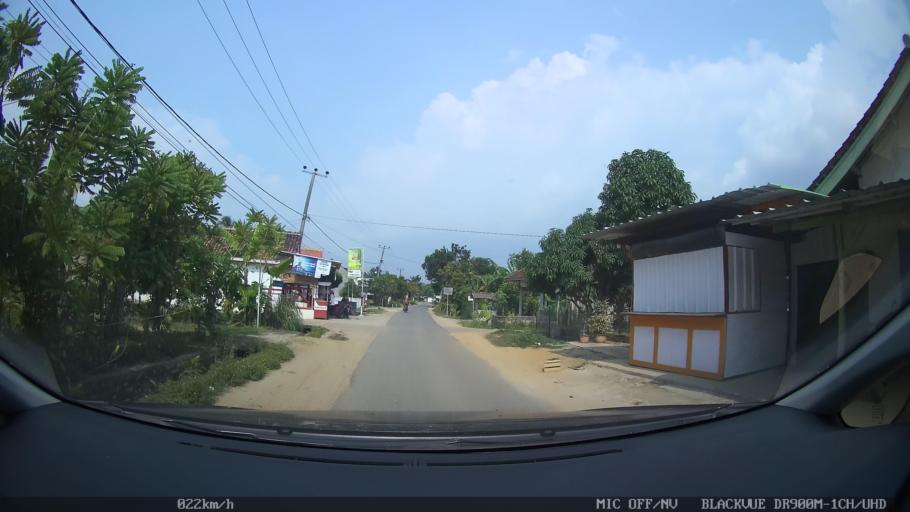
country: ID
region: Lampung
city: Kedondong
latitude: -5.4105
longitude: 104.9945
